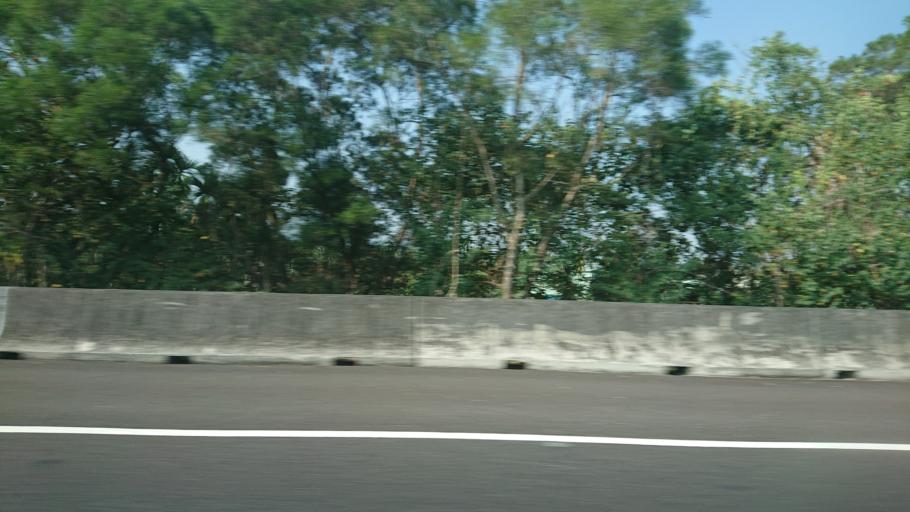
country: TW
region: Taiwan
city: Lugu
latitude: 23.8263
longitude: 120.7079
